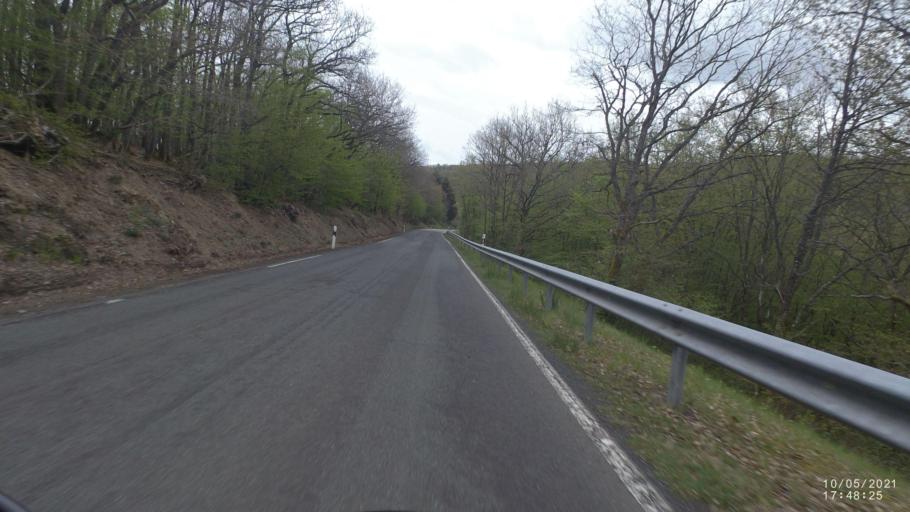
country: DE
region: Rheinland-Pfalz
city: Anschau
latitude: 50.2929
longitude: 7.1188
